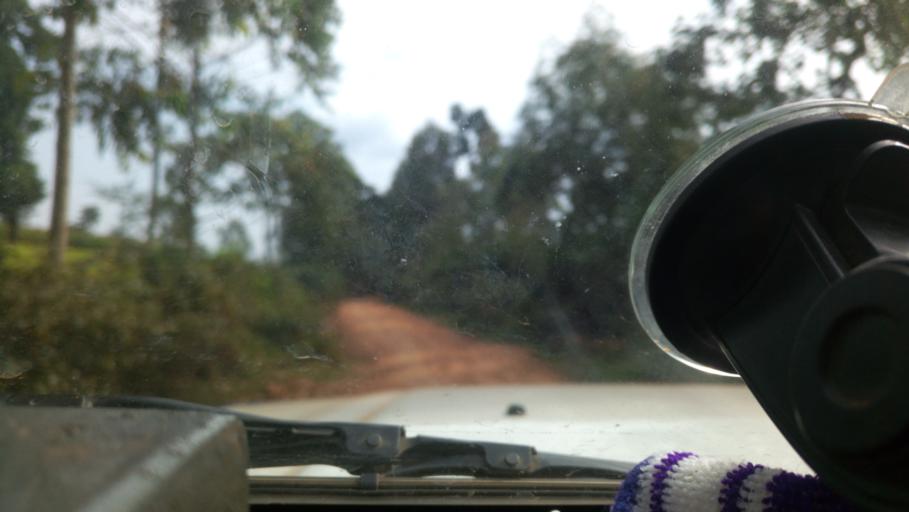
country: KE
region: Kericho
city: Litein
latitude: -0.5706
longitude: 35.2131
